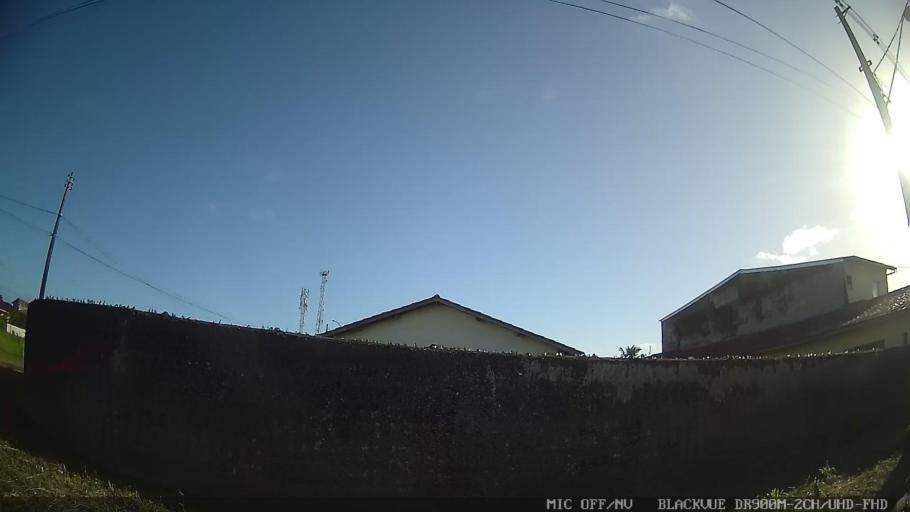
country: BR
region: Sao Paulo
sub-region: Itanhaem
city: Itanhaem
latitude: -24.1553
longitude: -46.7380
